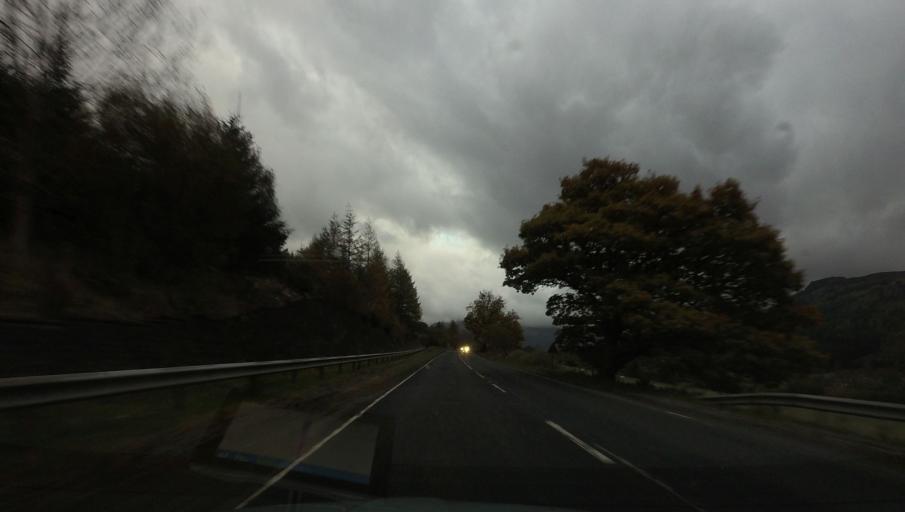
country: GB
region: Scotland
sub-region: Stirling
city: Callander
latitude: 56.3454
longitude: -4.3272
